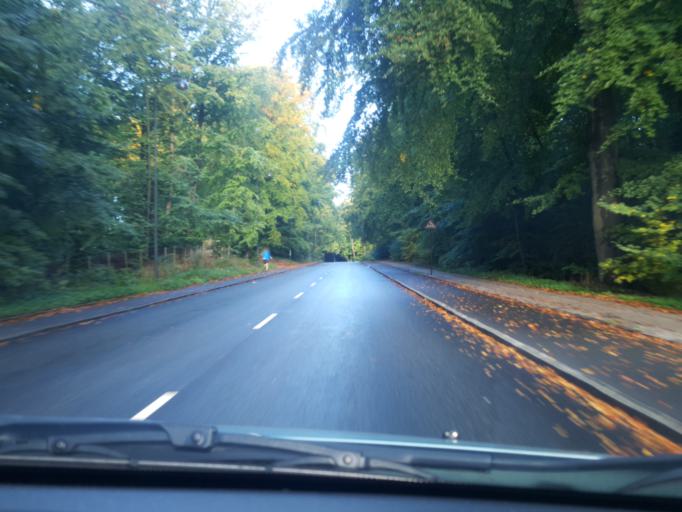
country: DK
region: Capital Region
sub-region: Gentofte Kommune
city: Charlottenlund
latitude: 55.7500
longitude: 12.5840
